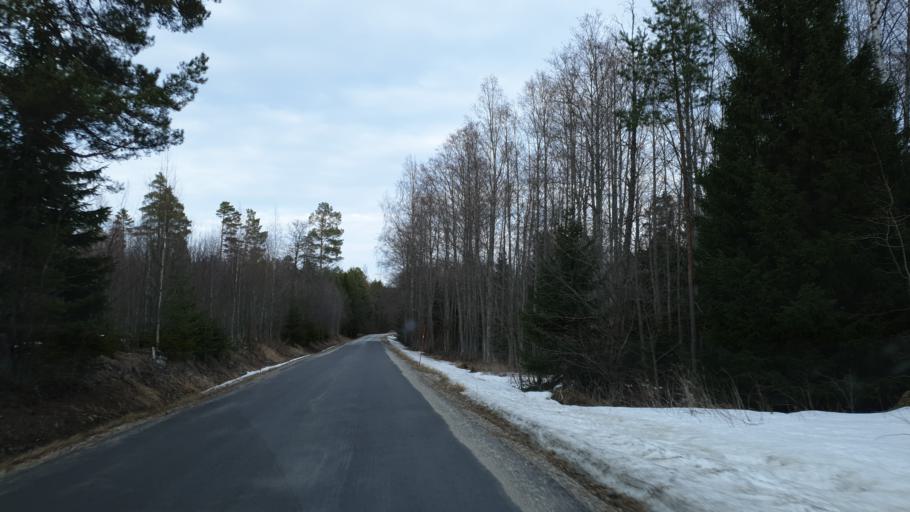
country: SE
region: Gaevleborg
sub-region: Nordanstigs Kommun
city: Bergsjoe
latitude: 61.9610
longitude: 17.3588
